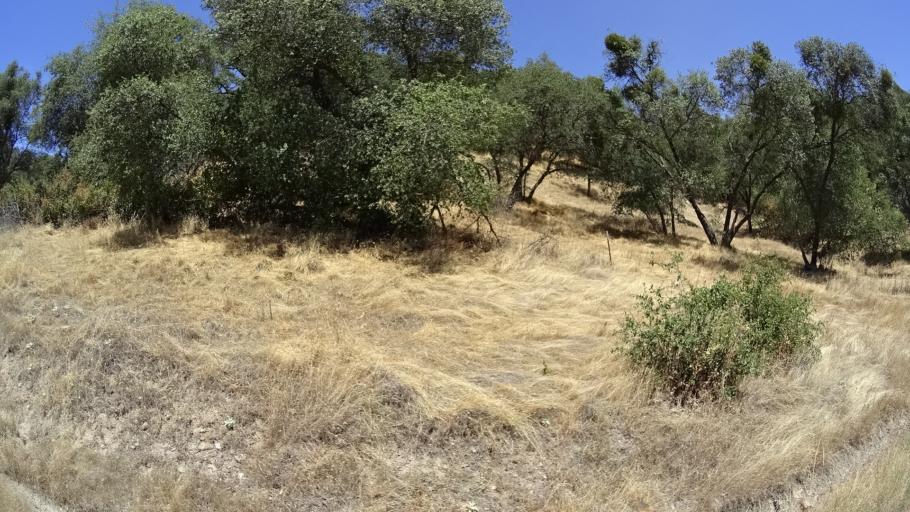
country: US
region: California
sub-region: Amador County
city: Jackson
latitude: 38.2931
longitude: -120.7152
